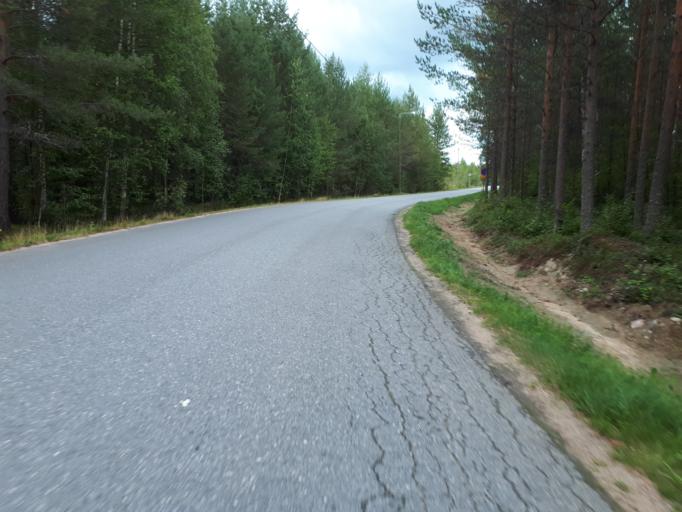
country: FI
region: Northern Ostrobothnia
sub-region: Oulunkaari
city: Ii
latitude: 65.3252
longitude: 25.3950
